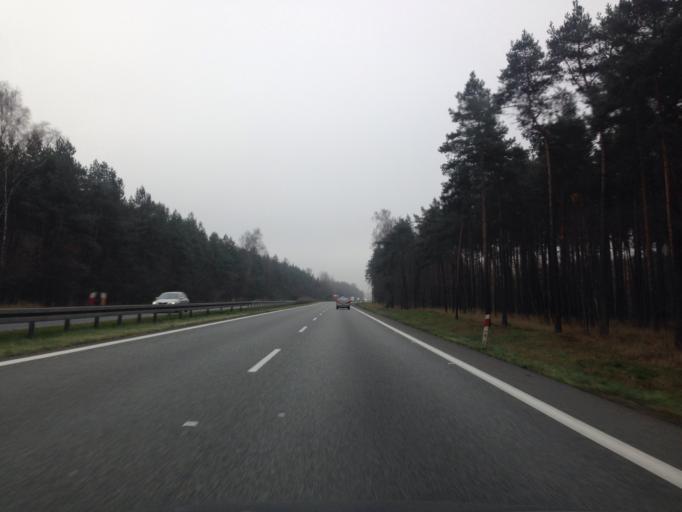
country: PL
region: Silesian Voivodeship
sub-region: Powiat bedzinski
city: Siewierz
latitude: 50.5283
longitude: 19.1915
